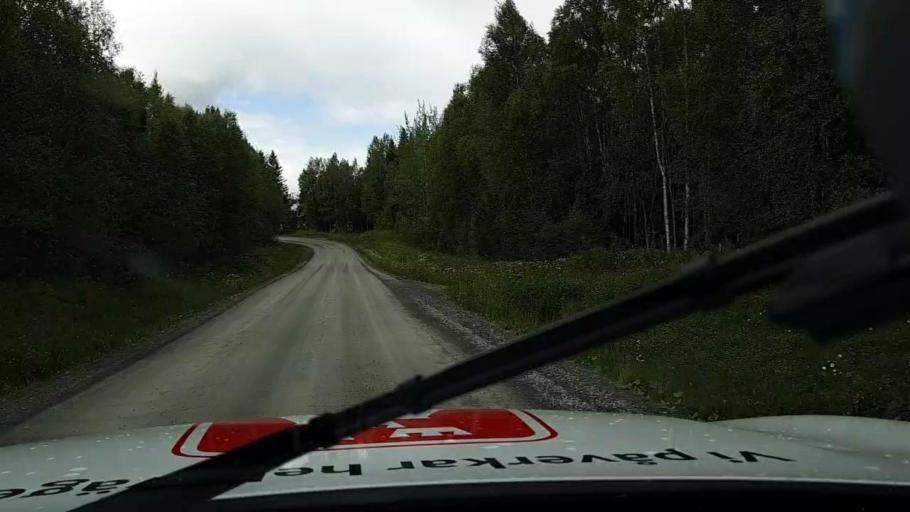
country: SE
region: Jaemtland
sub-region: Krokoms Kommun
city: Valla
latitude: 63.6618
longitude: 13.7554
